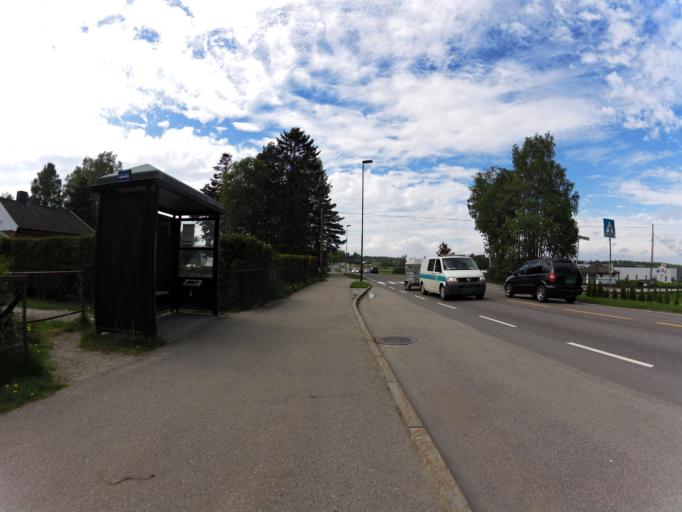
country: NO
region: Ostfold
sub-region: Rade
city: Karlshus
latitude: 59.3540
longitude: 10.8568
